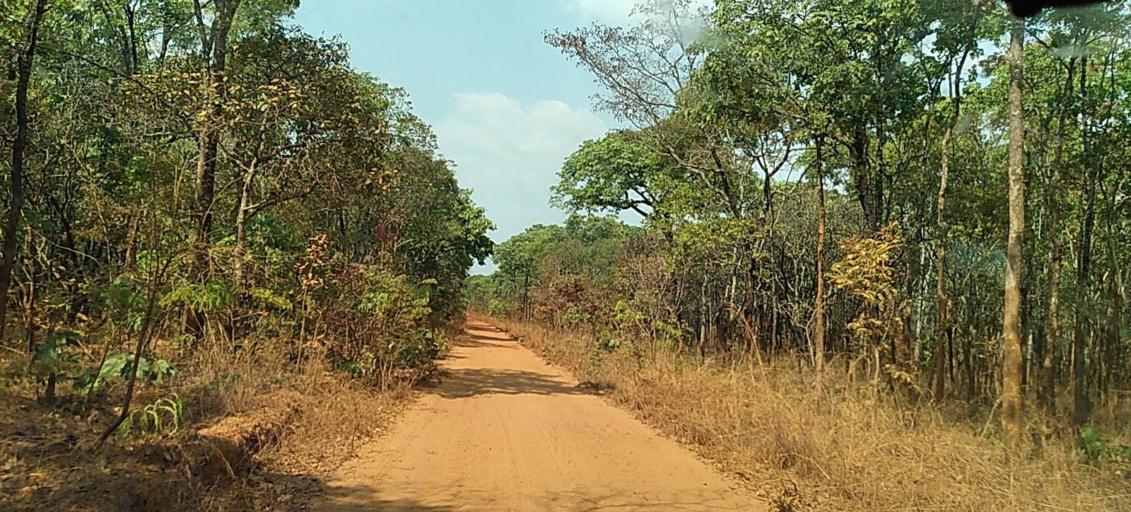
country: ZM
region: North-Western
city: Kasempa
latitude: -13.3183
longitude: 26.0531
